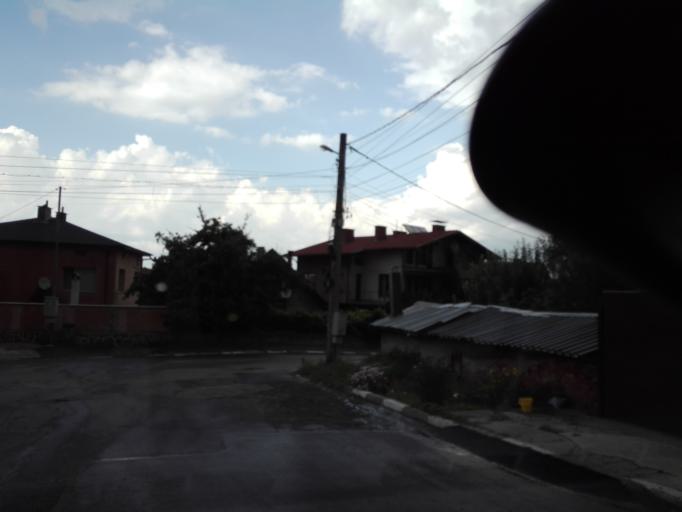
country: BG
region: Sofiya
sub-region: Obshtina Elin Pelin
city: Elin Pelin
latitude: 42.6002
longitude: 23.4783
